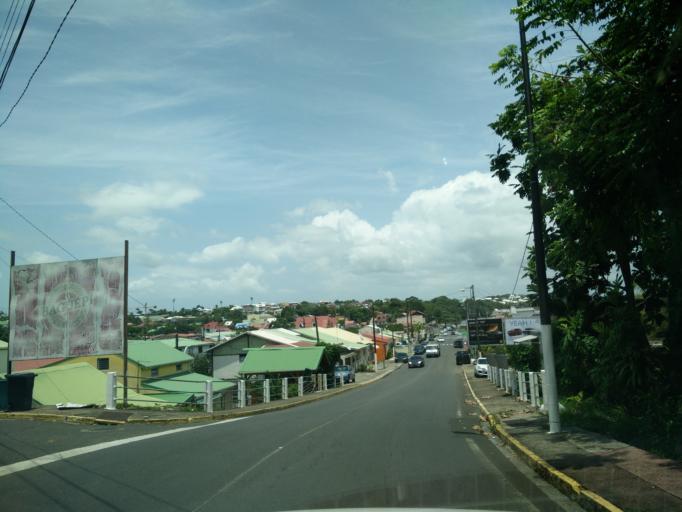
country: GP
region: Guadeloupe
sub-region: Guadeloupe
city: Petit-Bourg
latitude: 16.1897
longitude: -61.5912
